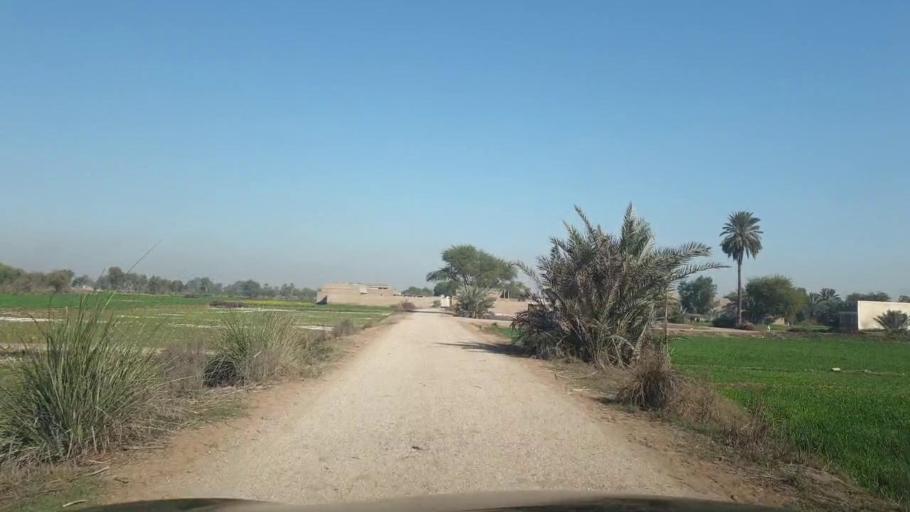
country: PK
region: Sindh
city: Ghotki
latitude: 27.9988
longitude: 69.3423
